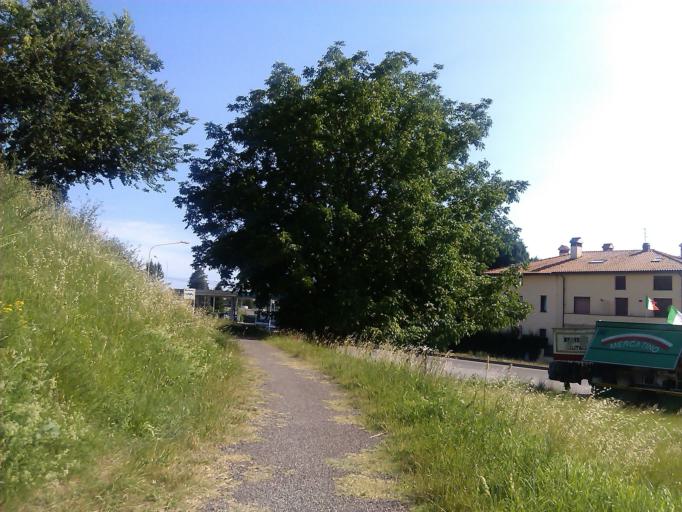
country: IT
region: Tuscany
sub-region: Province of Florence
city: Campi Bisenzio
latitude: 43.8571
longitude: 11.1230
